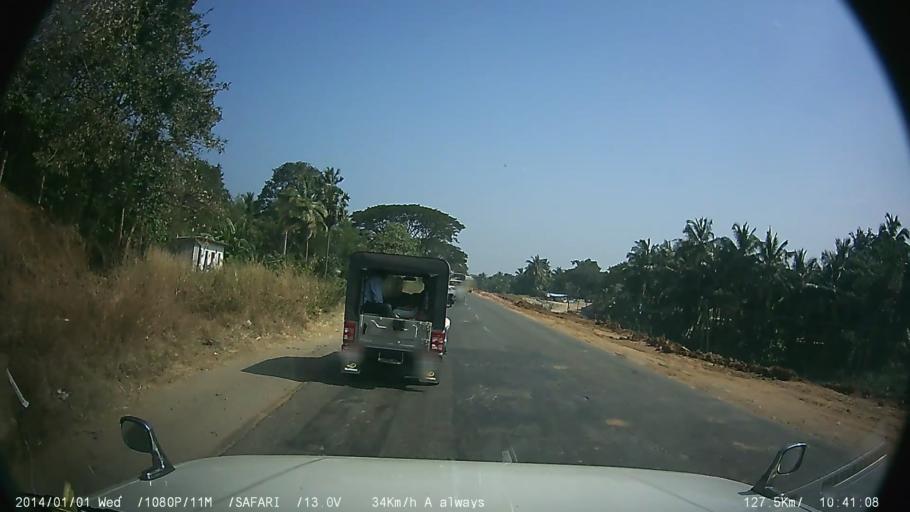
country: IN
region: Kerala
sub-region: Palakkad district
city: Palakkad
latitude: 10.6889
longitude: 76.5817
